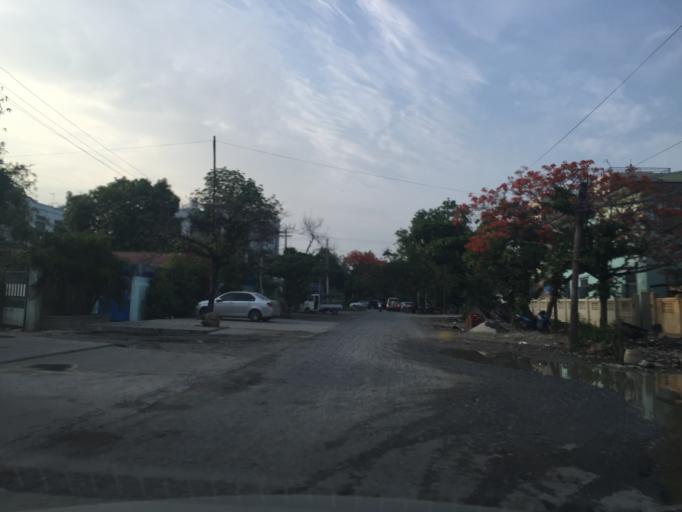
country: MM
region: Mandalay
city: Mandalay
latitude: 21.9721
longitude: 96.1014
